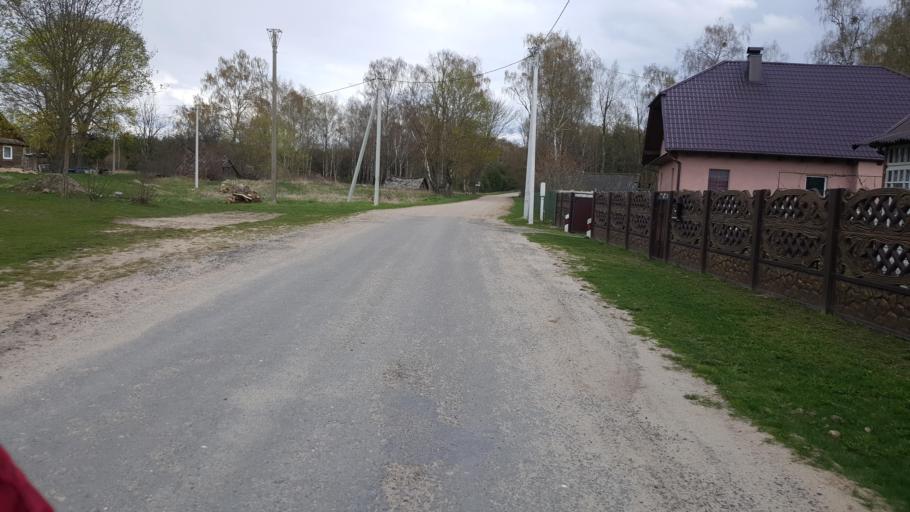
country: BY
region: Brest
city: Kamyanyets
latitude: 52.3995
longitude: 23.7342
